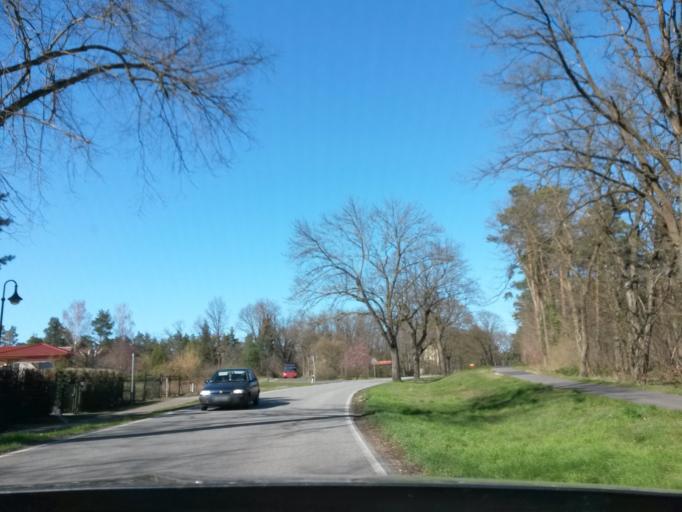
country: DE
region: Brandenburg
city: Rehfelde
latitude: 52.4666
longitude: 13.9061
